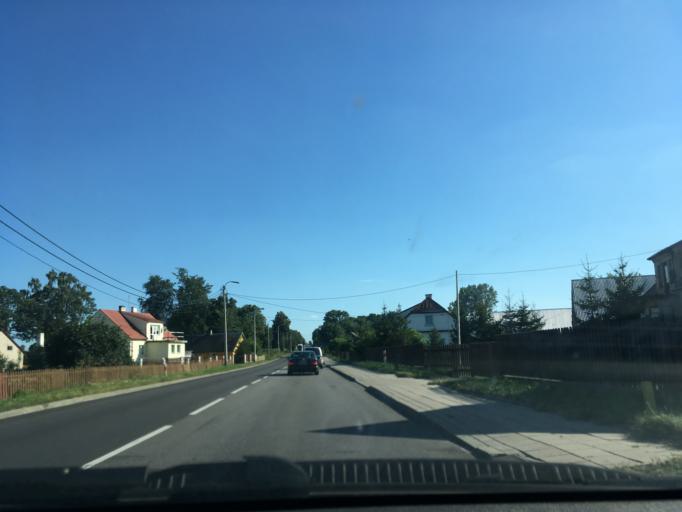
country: PL
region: Podlasie
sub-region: Powiat sokolski
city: Suchowola
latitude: 53.5394
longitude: 23.1038
